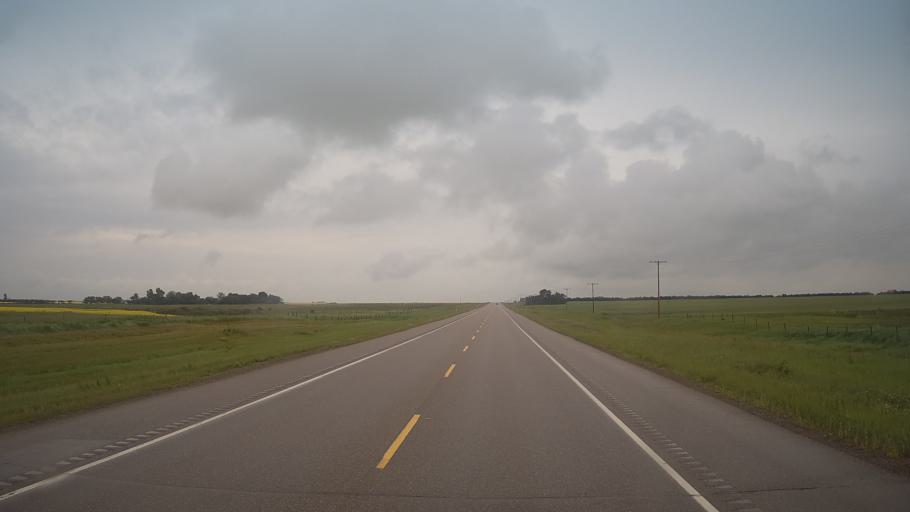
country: CA
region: Saskatchewan
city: Unity
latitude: 52.4348
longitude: -108.9400
